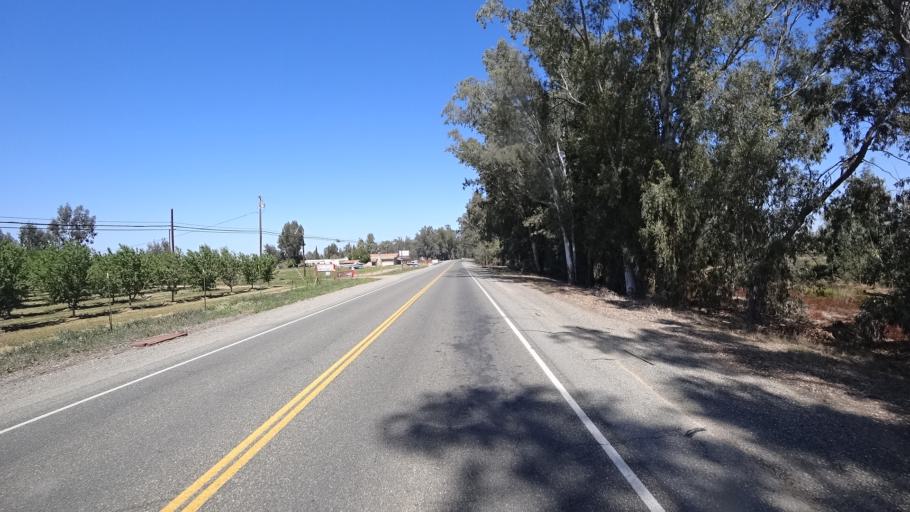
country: US
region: California
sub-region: Glenn County
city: Willows
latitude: 39.5919
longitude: -122.1947
